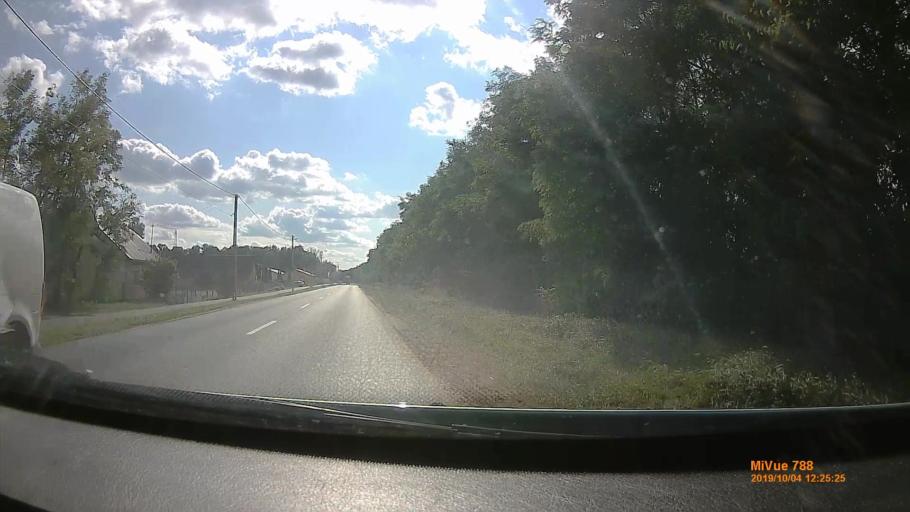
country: HU
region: Szabolcs-Szatmar-Bereg
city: Nyiregyhaza
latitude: 47.9864
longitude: 21.7043
